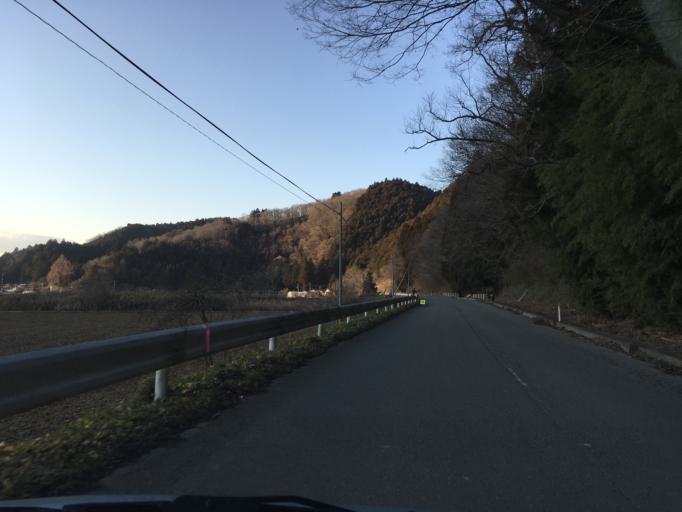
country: JP
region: Iwate
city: Ichinoseki
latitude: 38.8002
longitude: 141.2412
